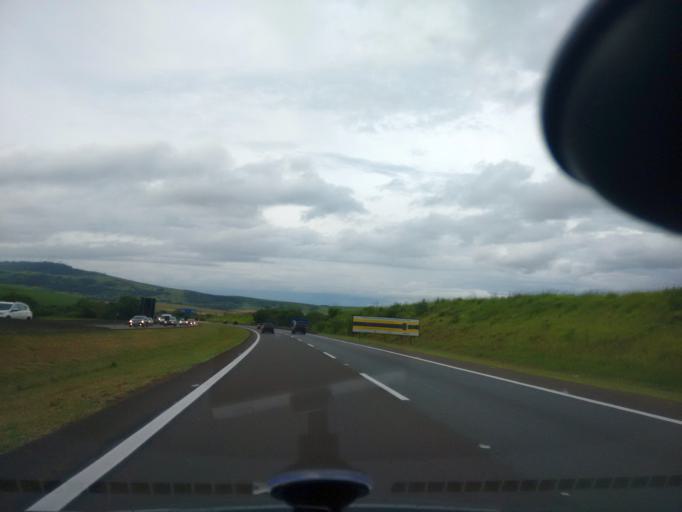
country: BR
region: Sao Paulo
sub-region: Limeira
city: Limeira
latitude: -22.5701
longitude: -47.4571
